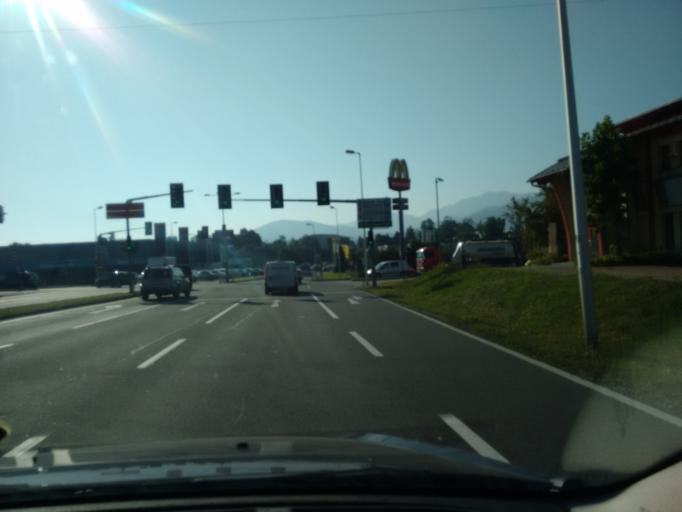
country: AT
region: Upper Austria
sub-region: Politischer Bezirk Gmunden
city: Gmunden
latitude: 47.9318
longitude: 13.7848
